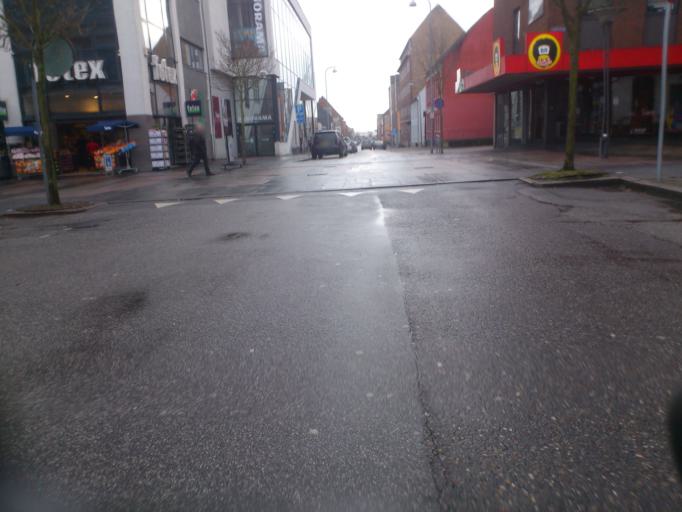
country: DK
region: South Denmark
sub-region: Fredericia Kommune
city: Fredericia
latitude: 55.5658
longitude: 9.7577
